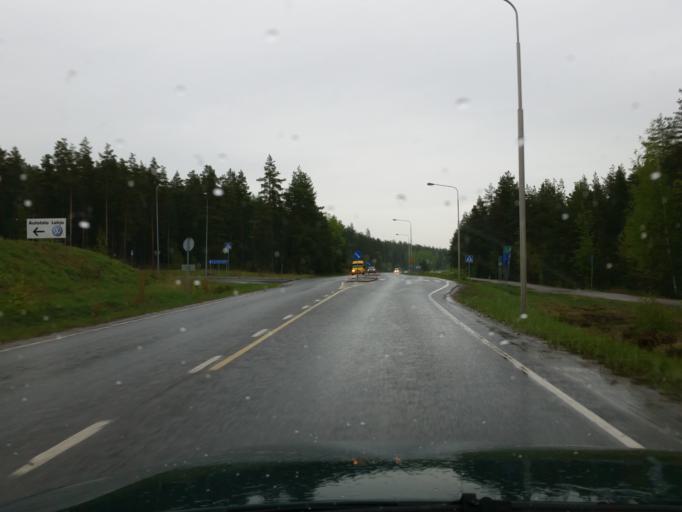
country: FI
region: Uusimaa
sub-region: Helsinki
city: Lohja
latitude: 60.2725
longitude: 24.1241
